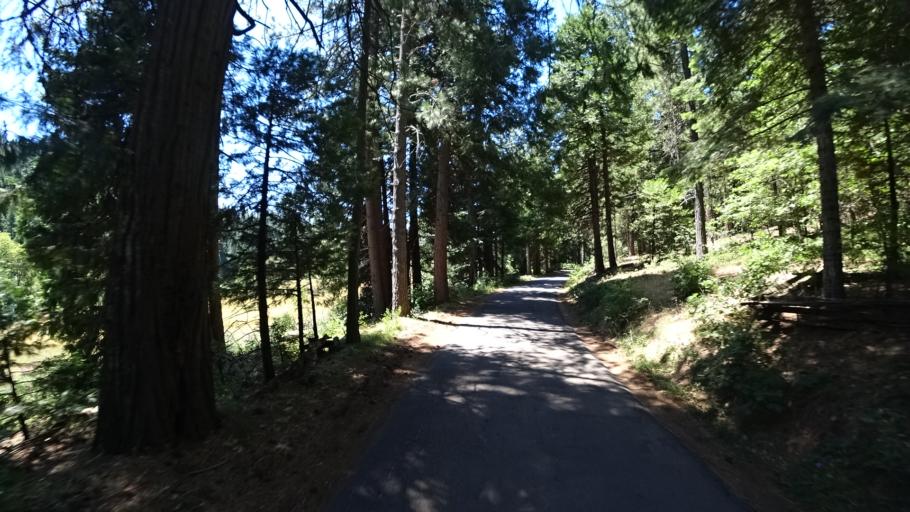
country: US
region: California
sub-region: Calaveras County
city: Arnold
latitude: 38.2278
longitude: -120.3253
